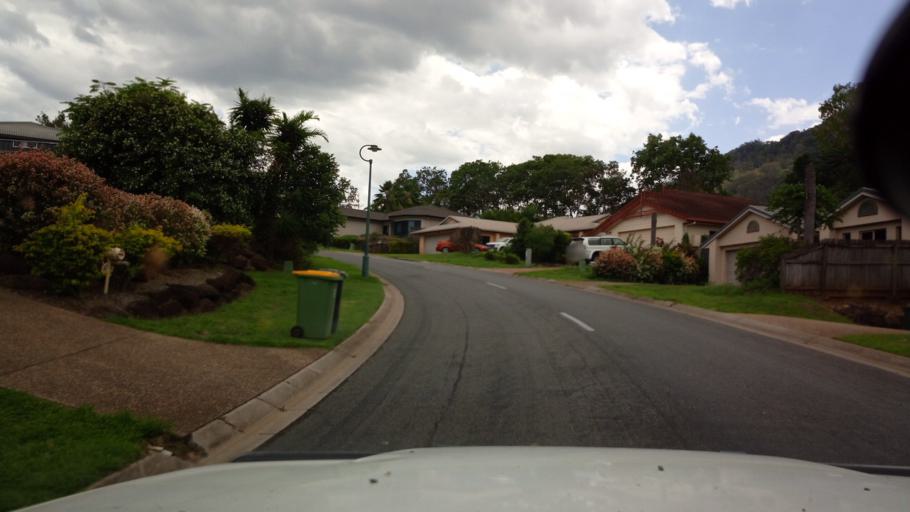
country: AU
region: Queensland
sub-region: Cairns
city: Redlynch
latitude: -16.9116
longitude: 145.7176
